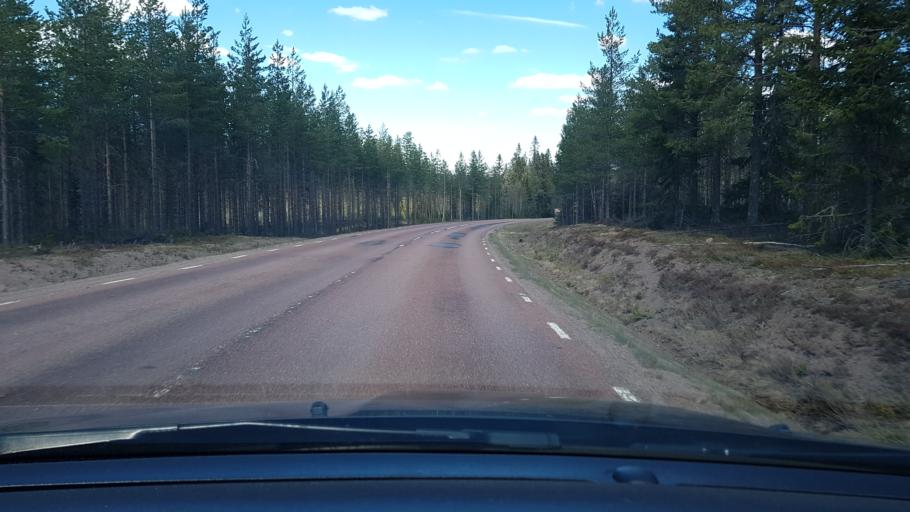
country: SE
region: Dalarna
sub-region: Malung-Saelens kommun
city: Malung
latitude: 61.0525
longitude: 13.3626
